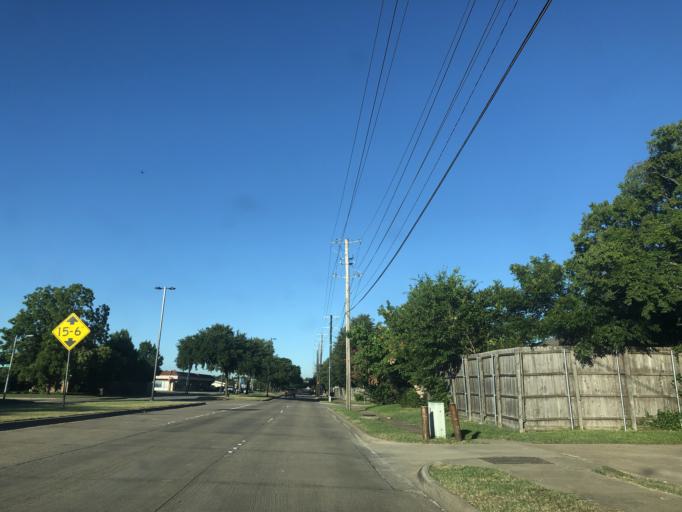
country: US
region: Texas
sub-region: Dallas County
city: Garland
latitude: 32.8494
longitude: -96.6282
